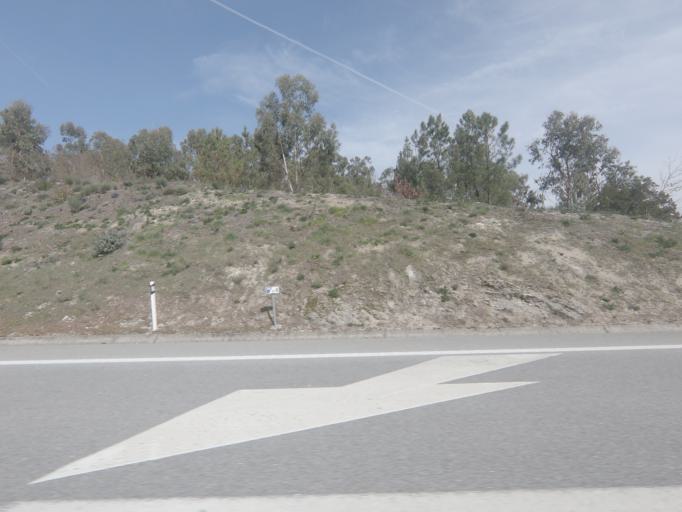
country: PT
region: Viseu
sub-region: Viseu
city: Viseu
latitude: 40.6321
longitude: -7.9747
